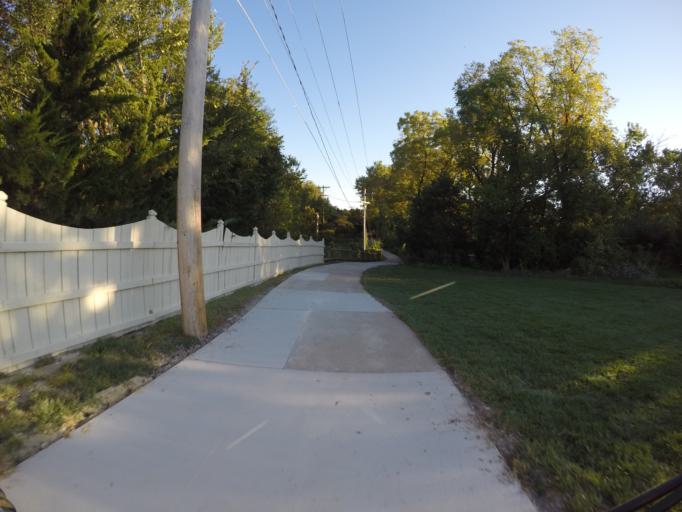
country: US
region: Kansas
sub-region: Riley County
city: Manhattan
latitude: 39.2109
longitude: -96.6260
